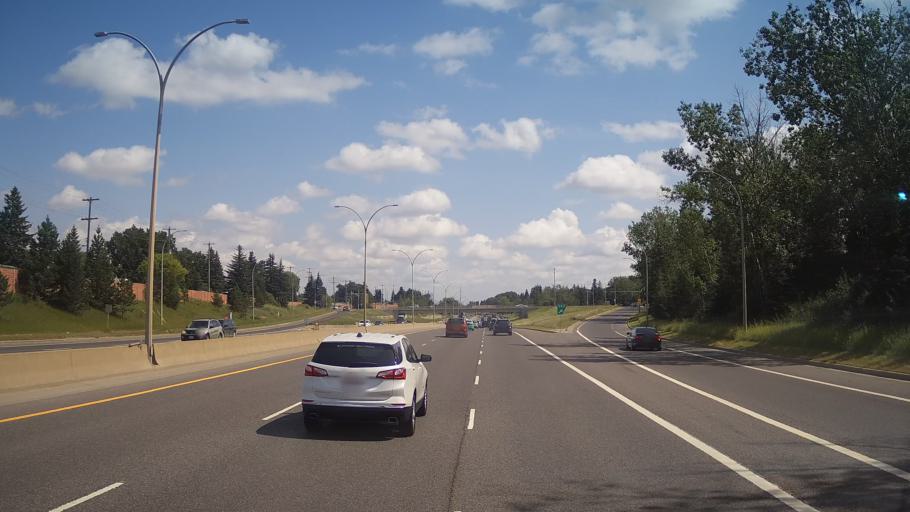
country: CA
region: Alberta
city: St. Albert
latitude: 53.5119
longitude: -113.6016
